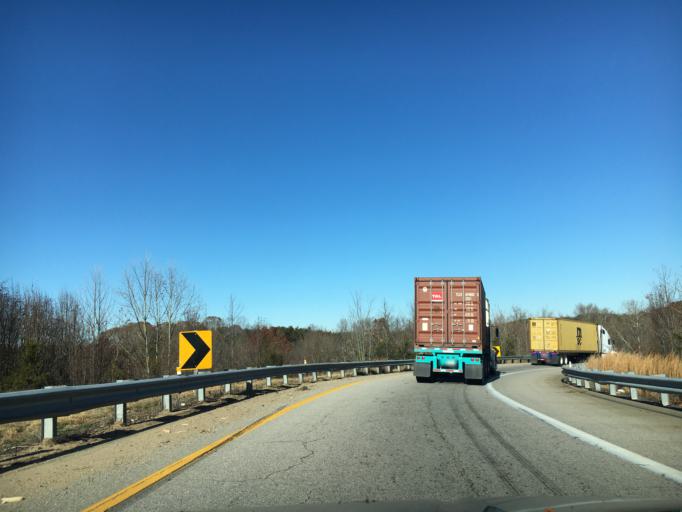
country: US
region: Virginia
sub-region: Pittsylvania County
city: Mount Hermon
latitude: 36.6063
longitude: -79.5371
